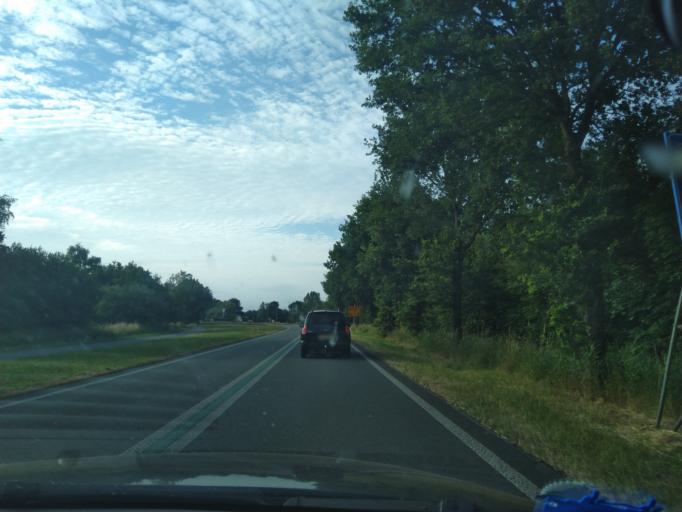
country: NL
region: Groningen
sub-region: Gemeente  Oldambt
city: Winschoten
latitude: 53.1093
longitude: 7.0669
